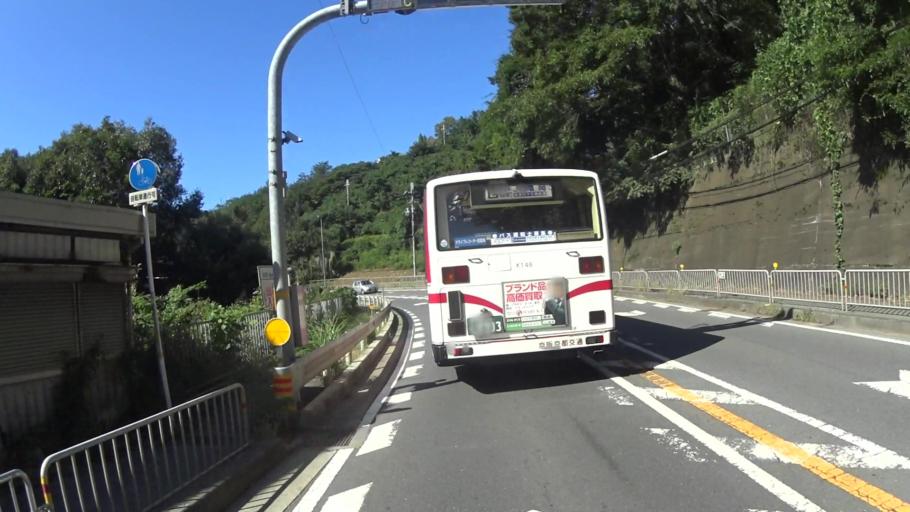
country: JP
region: Kyoto
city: Muko
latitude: 34.9791
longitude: 135.6520
